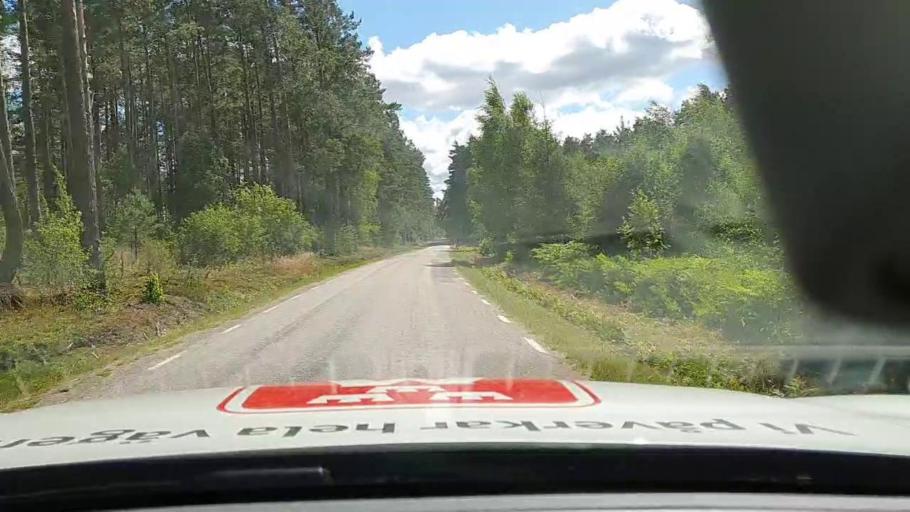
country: SE
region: Vaestra Goetaland
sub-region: Toreboda Kommun
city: Toereboda
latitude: 58.5790
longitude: 14.1237
